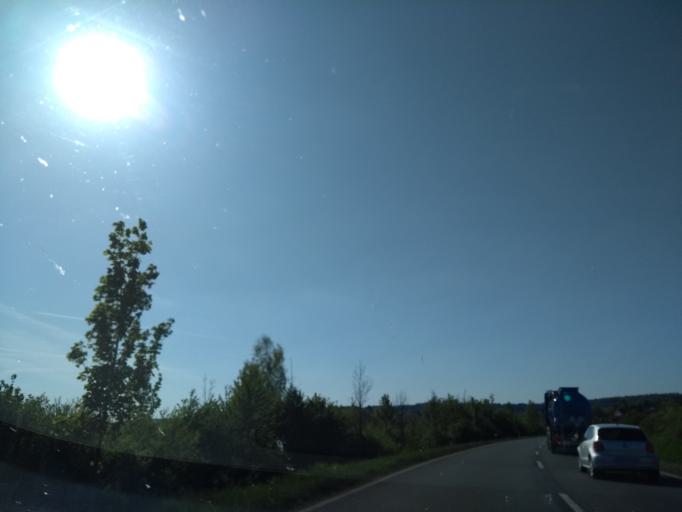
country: DE
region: Hesse
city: Frankenberg
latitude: 51.0420
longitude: 8.7542
